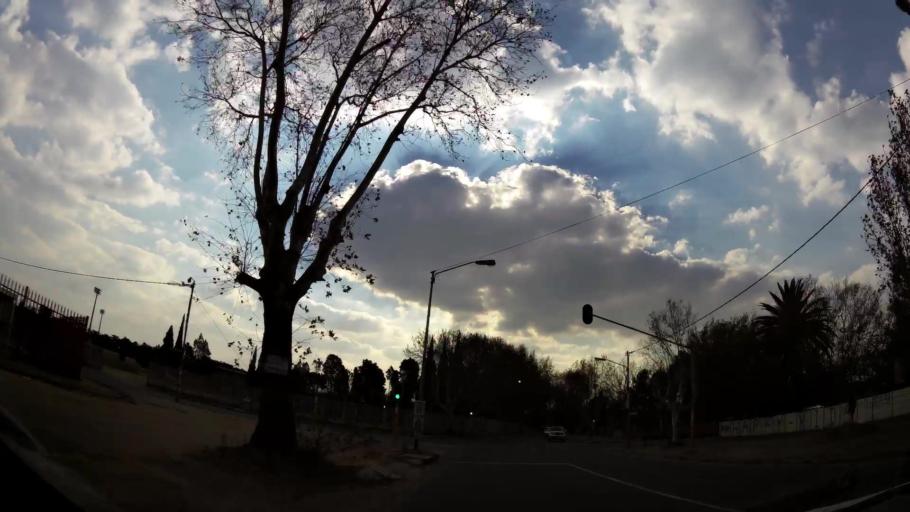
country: ZA
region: Gauteng
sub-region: Ekurhuleni Metropolitan Municipality
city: Germiston
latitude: -26.2273
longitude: 28.1784
